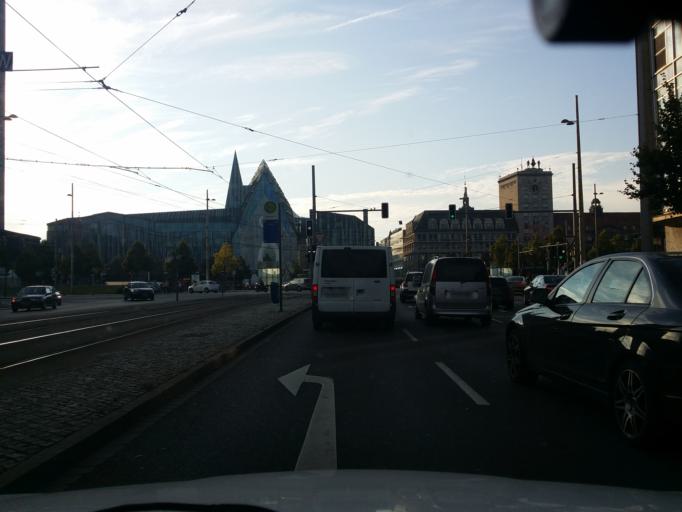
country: DE
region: Saxony
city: Leipzig
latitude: 51.3386
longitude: 12.3829
